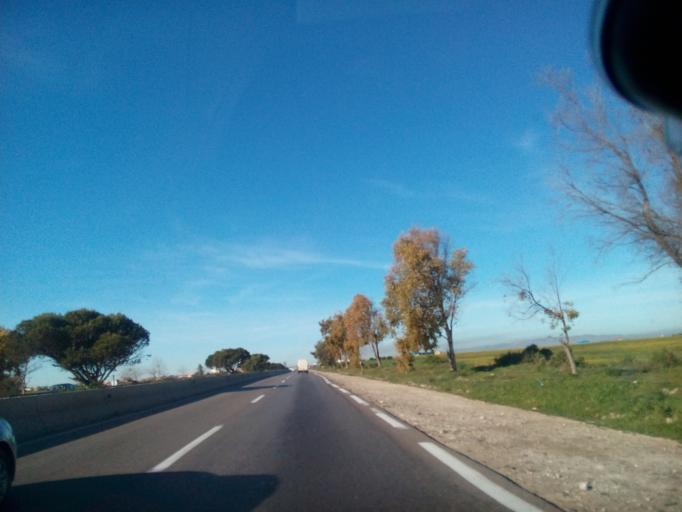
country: DZ
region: Oran
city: Ain el Bya
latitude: 35.7668
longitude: -0.2115
